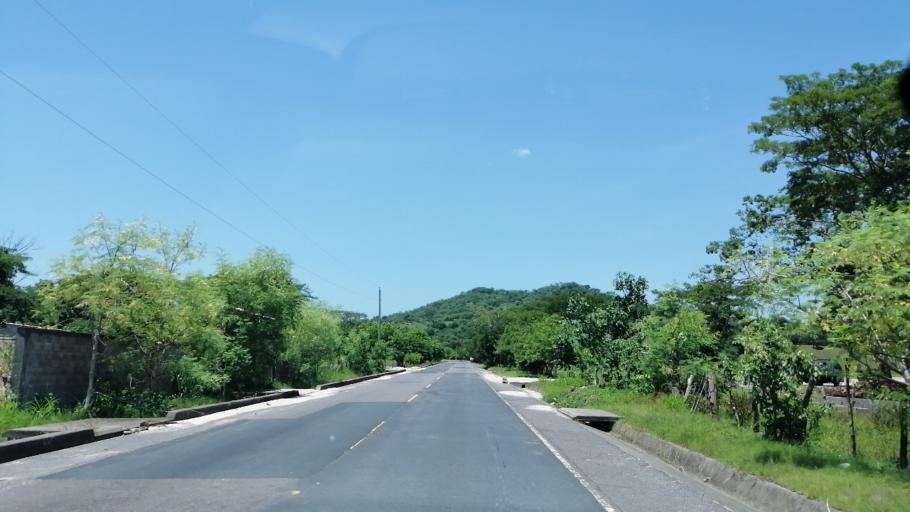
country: SV
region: Chalatenango
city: Chalatenango
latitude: 14.0330
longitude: -88.9604
